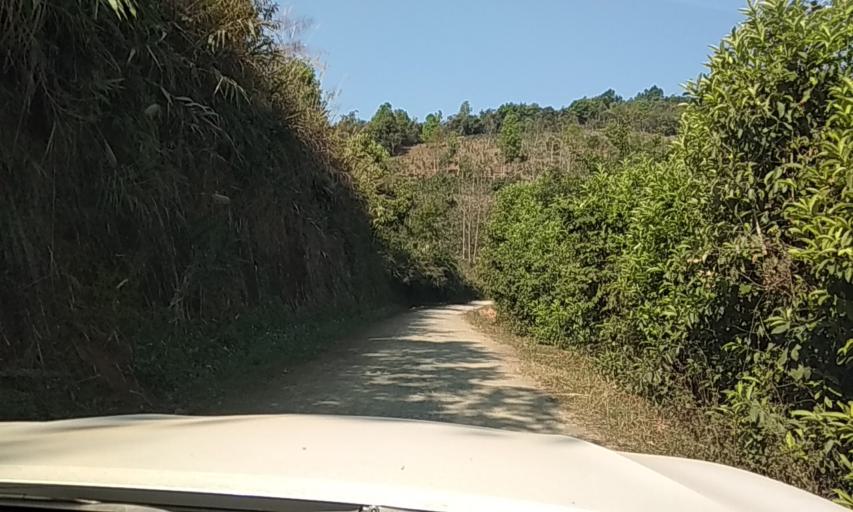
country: LA
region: Phongsali
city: Phongsali
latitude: 21.6953
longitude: 102.0843
